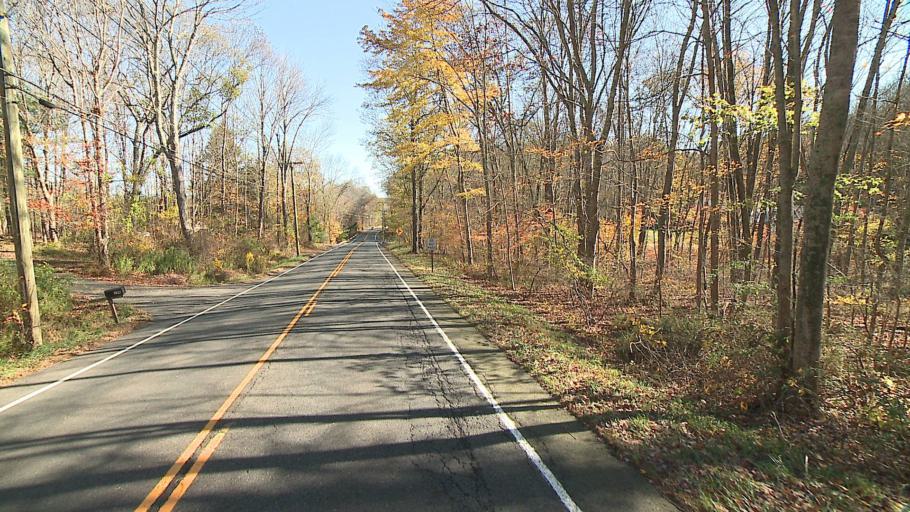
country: US
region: Connecticut
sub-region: Tolland County
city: Coventry Lake
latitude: 41.7987
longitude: -72.3197
